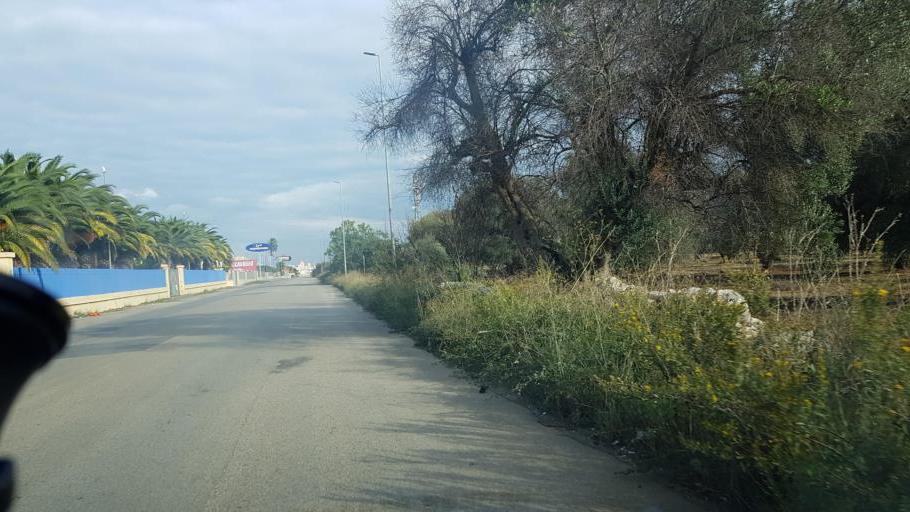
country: IT
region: Apulia
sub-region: Provincia di Brindisi
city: Francavilla Fontana
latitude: 40.5326
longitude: 17.5497
